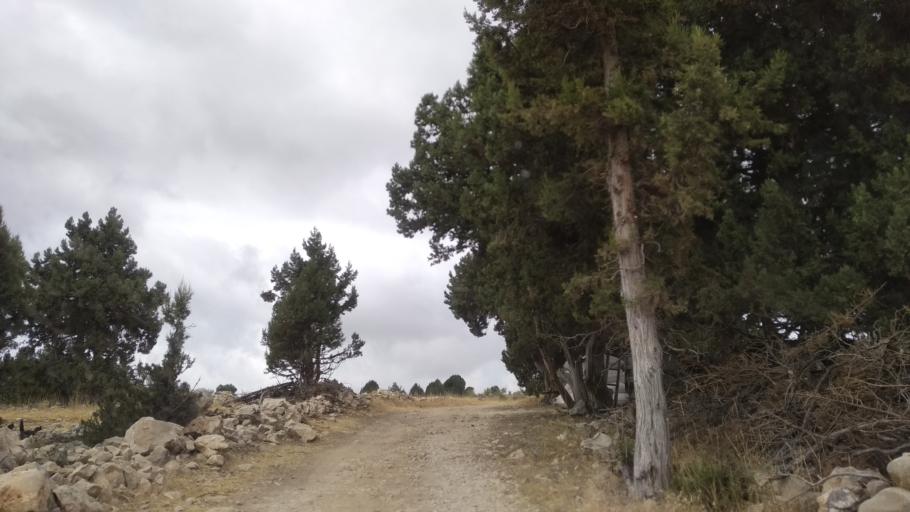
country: TR
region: Mersin
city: Sarikavak
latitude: 36.5649
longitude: 33.7694
